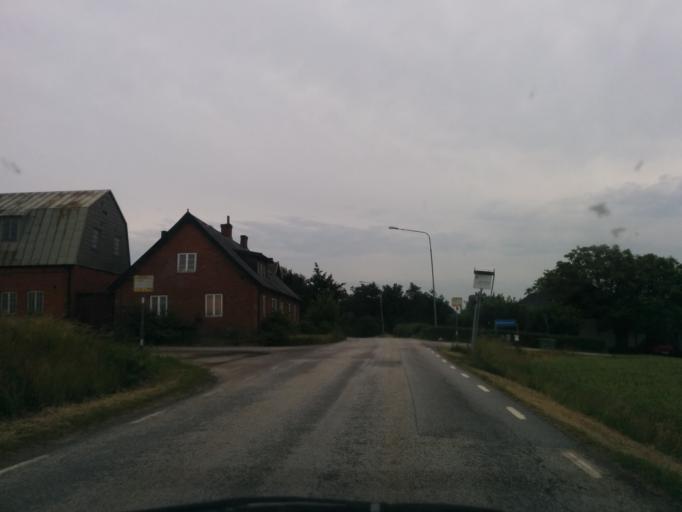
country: SE
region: Skane
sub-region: Lunds Kommun
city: Genarp
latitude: 55.6425
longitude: 13.3522
